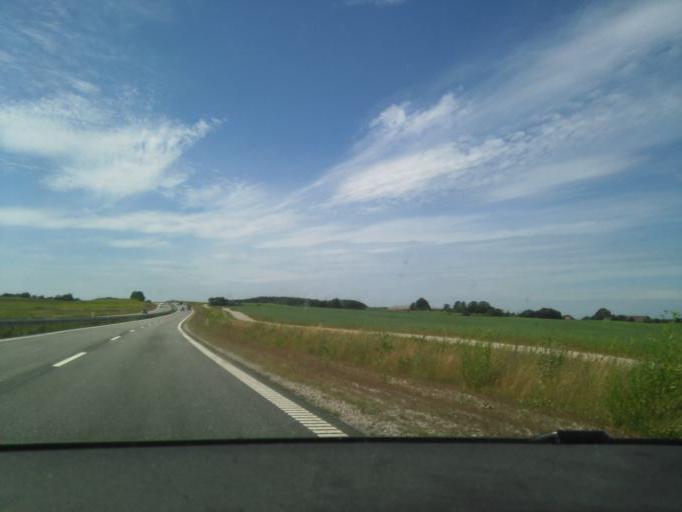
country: DK
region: Zealand
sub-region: Holbaek Kommune
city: Vipperod
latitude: 55.6451
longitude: 11.7460
